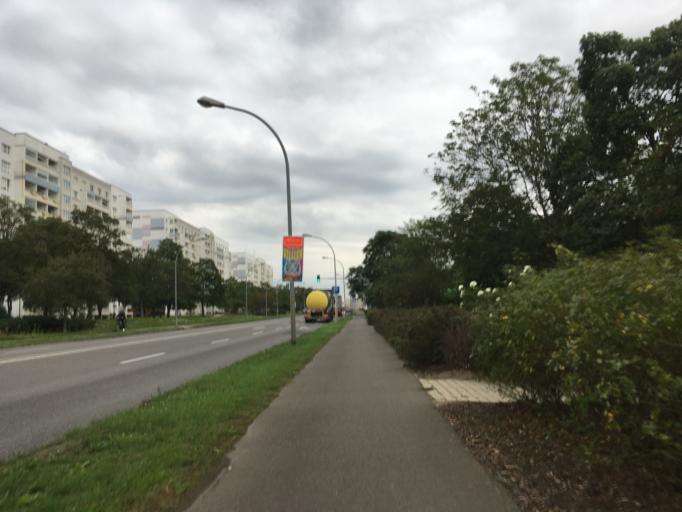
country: DE
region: Brandenburg
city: Schwedt (Oder)
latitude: 53.0630
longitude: 14.2825
